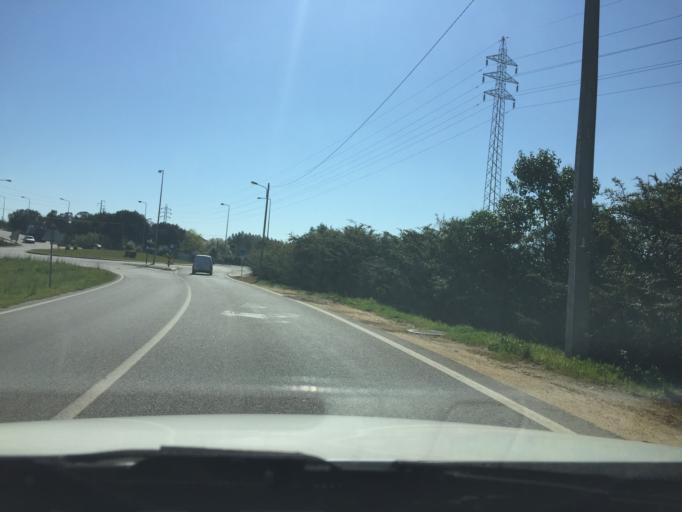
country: PT
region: Aveiro
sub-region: Anadia
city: Arcos
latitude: 40.4449
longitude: -8.4592
